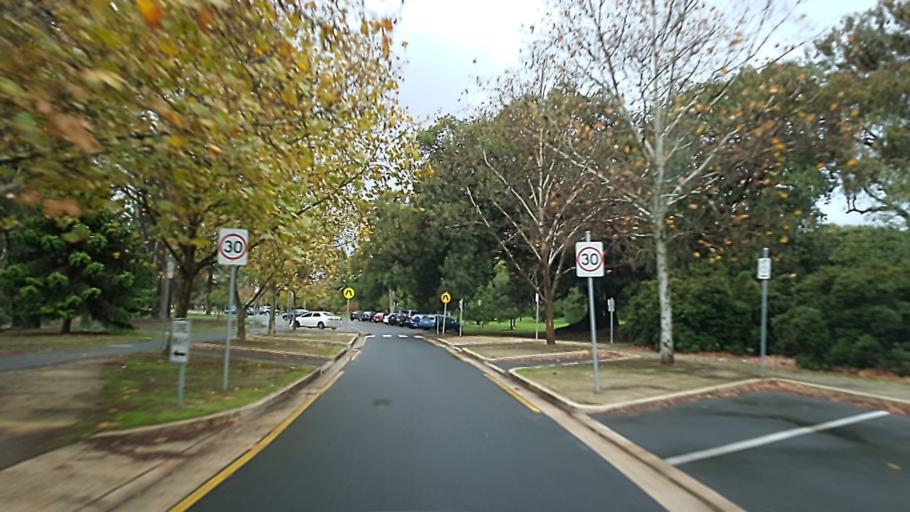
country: AU
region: South Australia
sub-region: Adelaide
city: Adelaide
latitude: -34.9134
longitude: 138.6097
